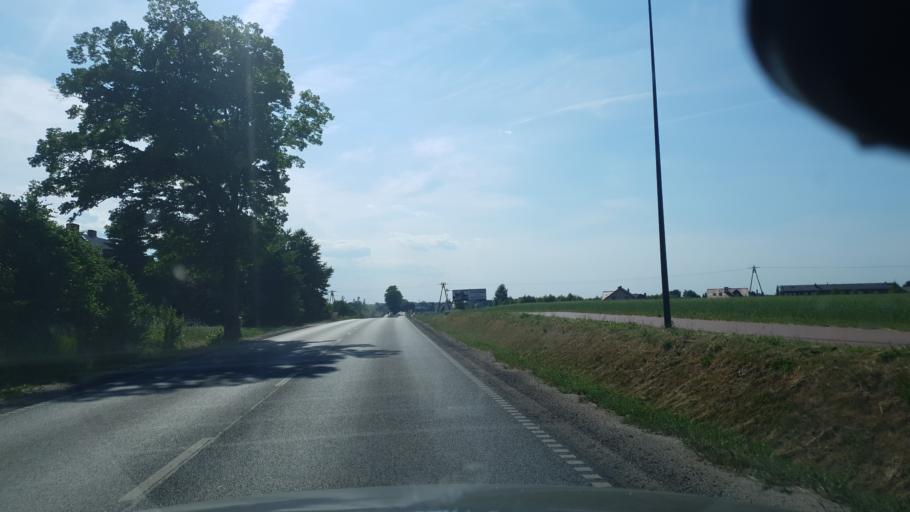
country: PL
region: Pomeranian Voivodeship
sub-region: Powiat kartuski
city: Chwaszczyno
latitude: 54.4427
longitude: 18.4365
